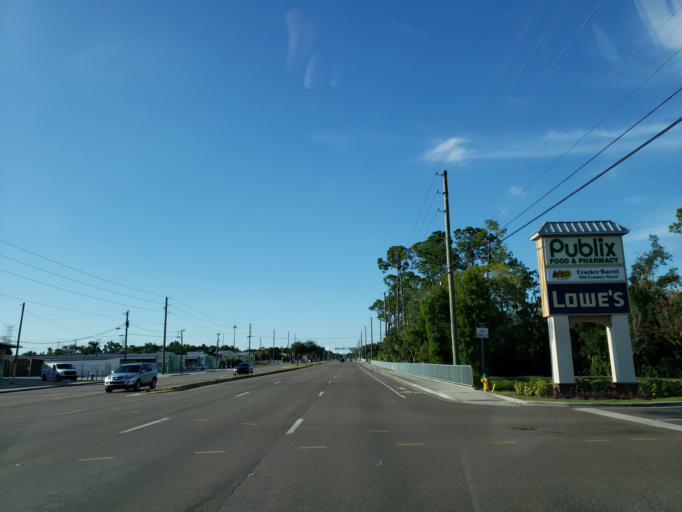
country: US
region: Florida
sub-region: Pinellas County
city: Oldsmar
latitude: 28.0360
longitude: -82.6483
